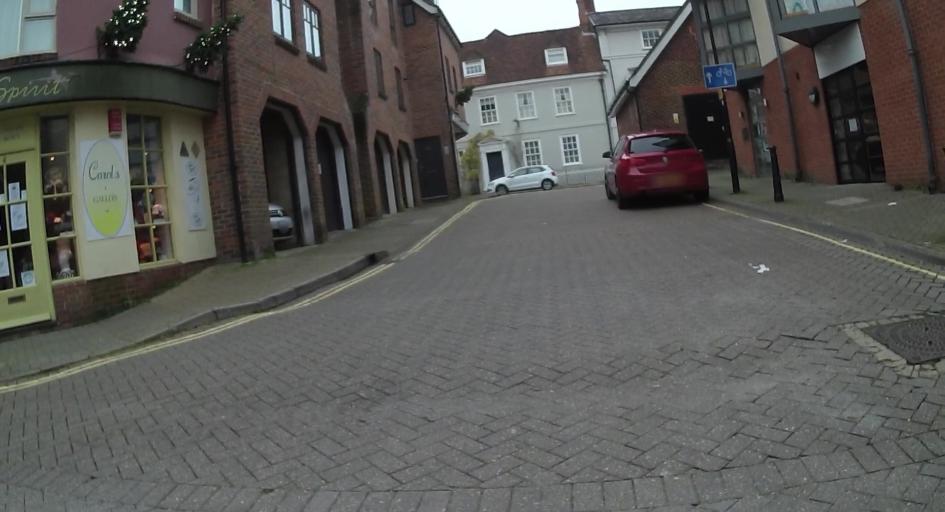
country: GB
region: England
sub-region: Hampshire
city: Winchester
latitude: 51.0621
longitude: -1.3156
